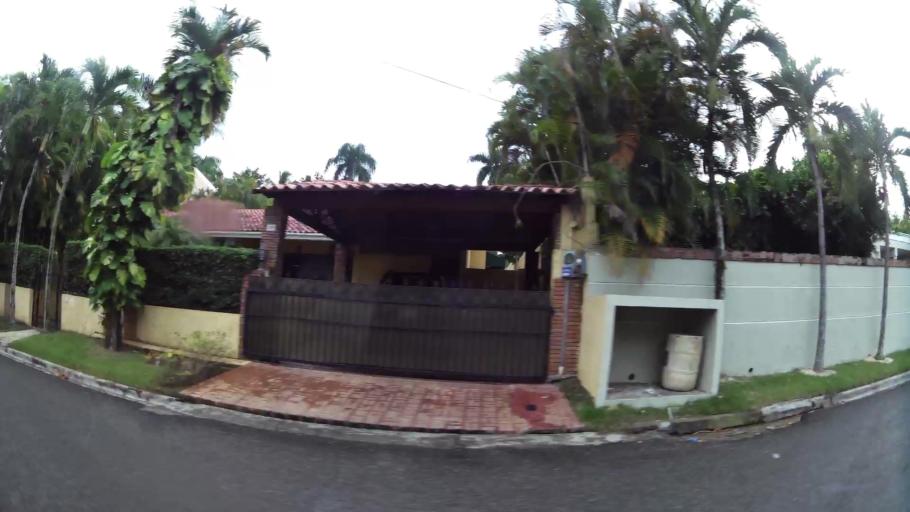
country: DO
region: Nacional
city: La Agustina
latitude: 18.5103
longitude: -69.9500
